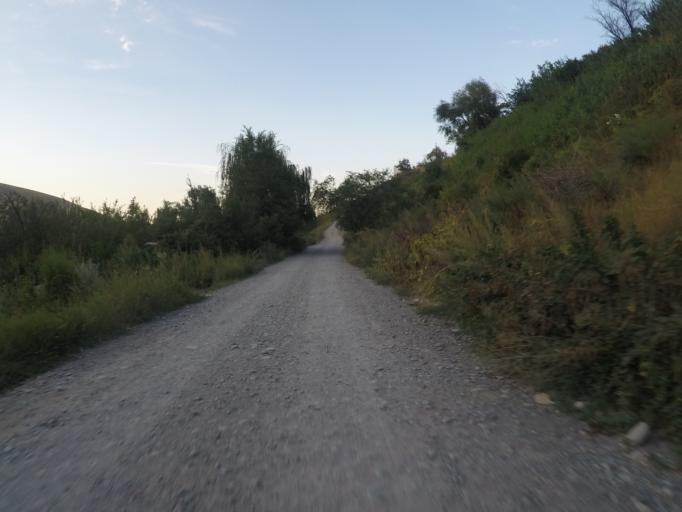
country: KG
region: Chuy
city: Bishkek
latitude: 42.7767
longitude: 74.6440
